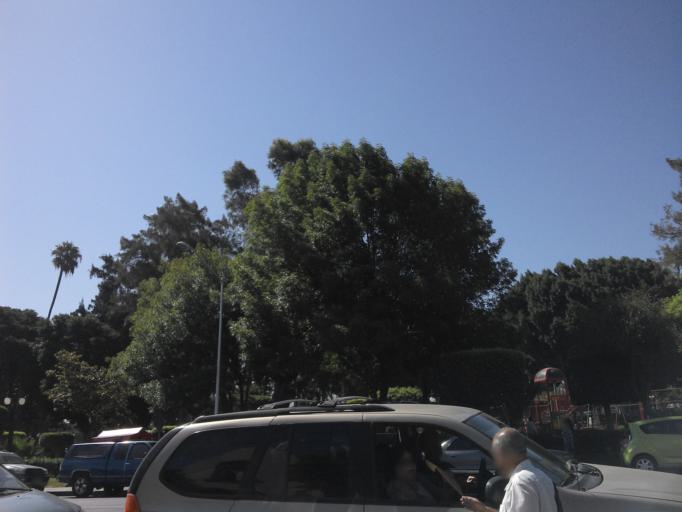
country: MX
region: Baja California
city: Tijuana
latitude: 32.5333
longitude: -117.0462
